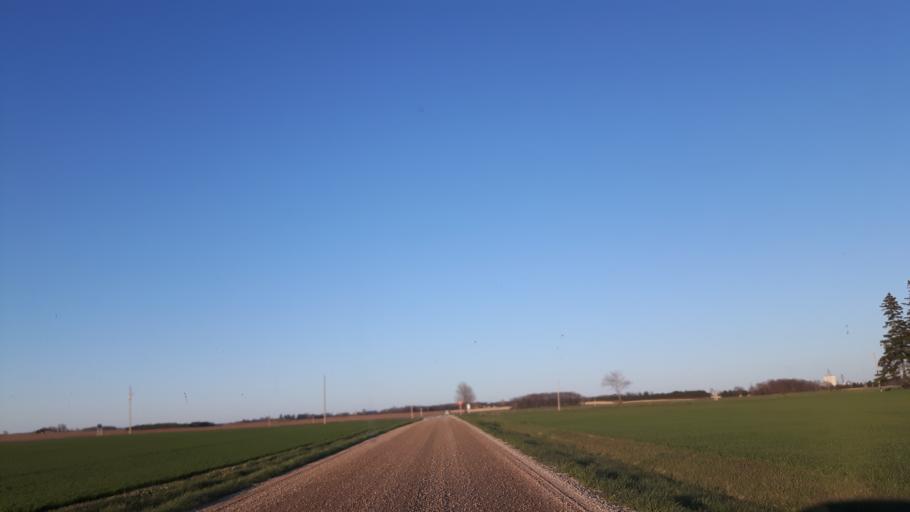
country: CA
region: Ontario
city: Bluewater
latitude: 43.5617
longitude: -81.5261
